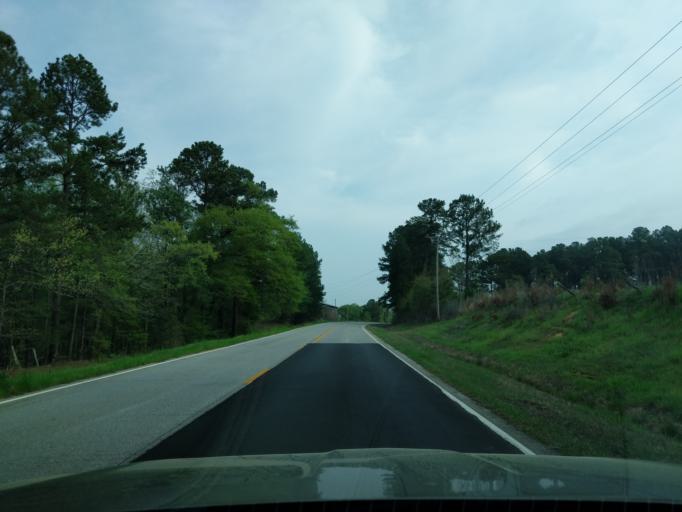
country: US
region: Georgia
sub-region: Lincoln County
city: Lincolnton
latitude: 33.8157
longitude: -82.4086
